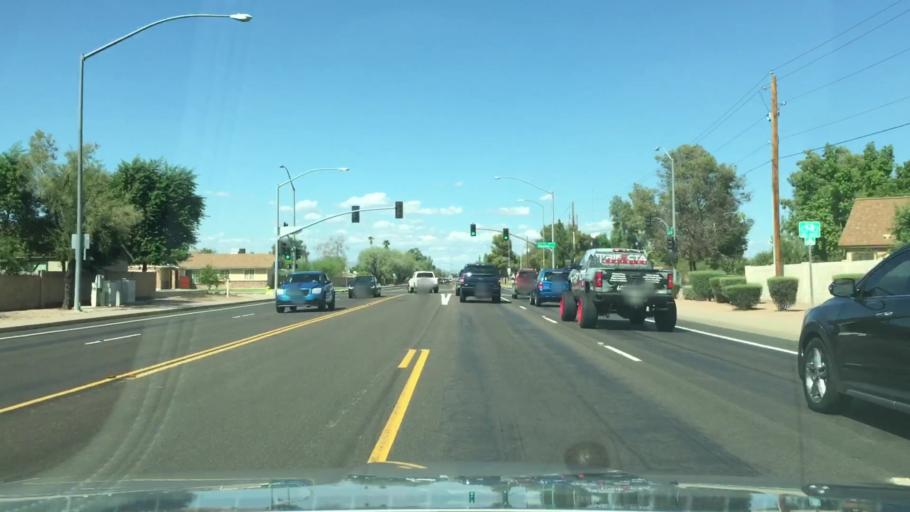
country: US
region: Arizona
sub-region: Maricopa County
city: Gilbert
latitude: 33.3999
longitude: -111.7534
